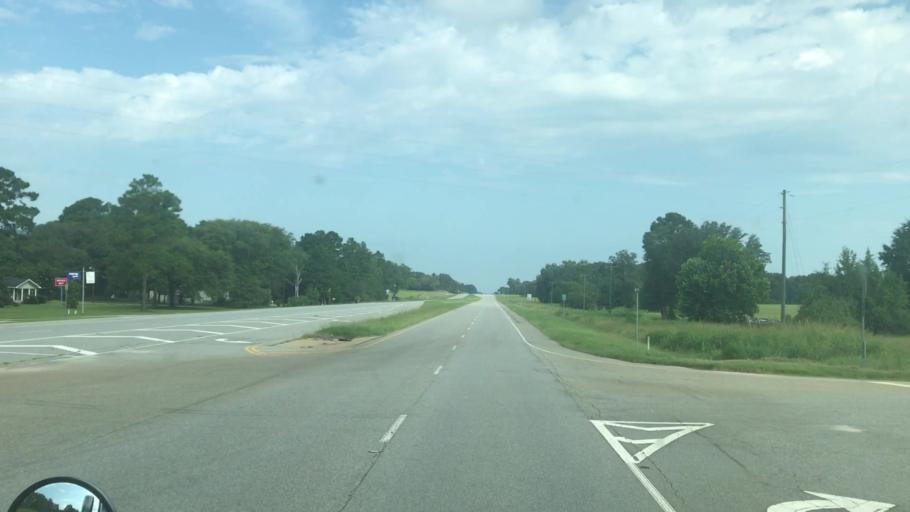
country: US
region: Georgia
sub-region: Early County
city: Blakely
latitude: 31.3037
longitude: -84.8633
